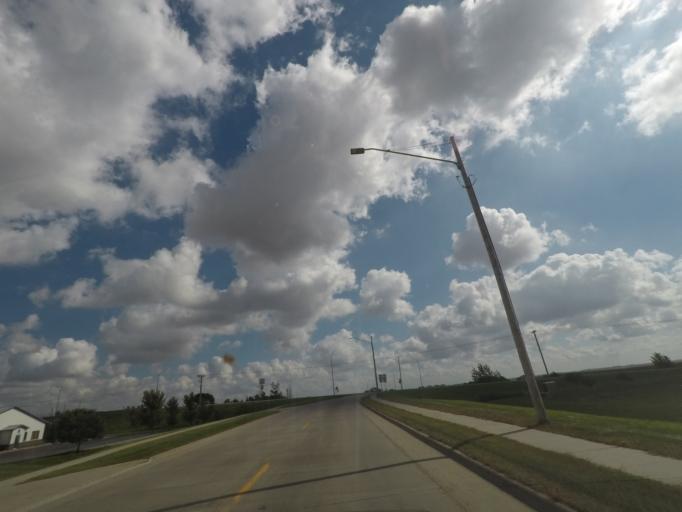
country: US
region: Iowa
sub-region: Story County
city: Nevada
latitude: 42.0062
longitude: -93.4365
